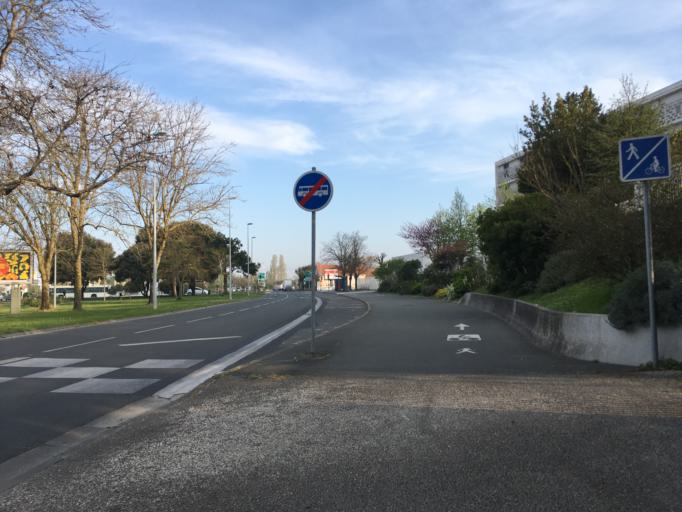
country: FR
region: Poitou-Charentes
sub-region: Departement de la Charente-Maritime
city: La Rochelle
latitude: 46.1764
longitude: -1.1508
